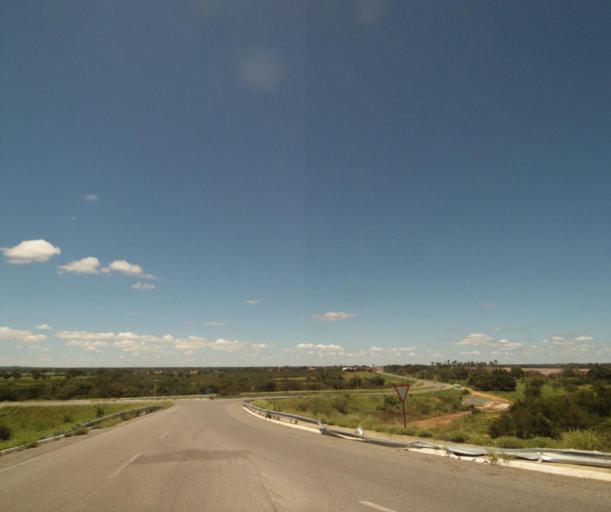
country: BR
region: Bahia
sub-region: Carinhanha
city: Carinhanha
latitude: -14.3279
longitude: -43.7652
